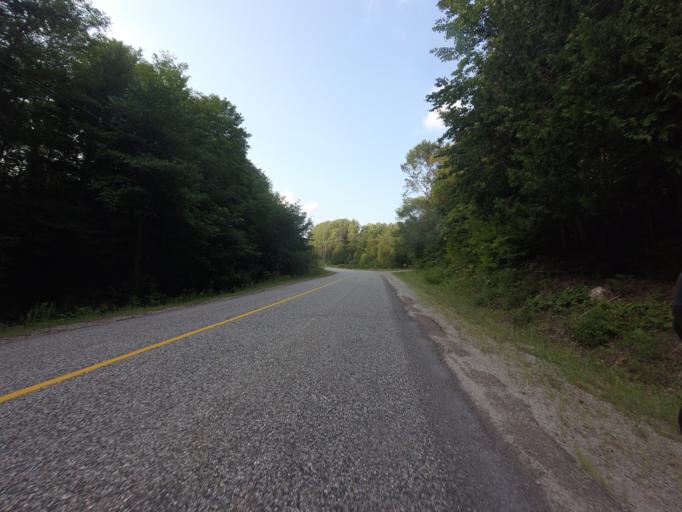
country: CA
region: Ontario
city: Renfrew
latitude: 44.9817
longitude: -76.7407
